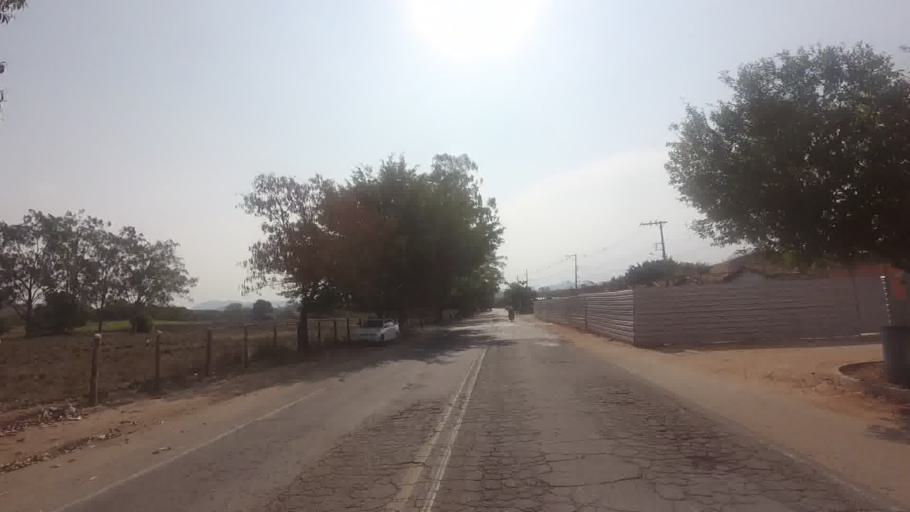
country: BR
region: Rio de Janeiro
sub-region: Bom Jesus Do Itabapoana
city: Bom Jesus do Itabapoana
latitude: -21.1480
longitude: -41.5782
